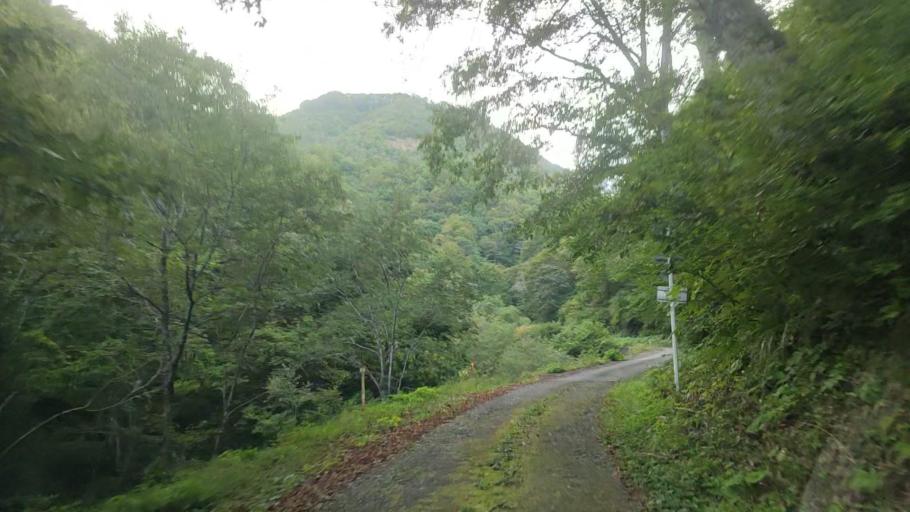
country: JP
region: Toyama
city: Yatsuomachi-higashikumisaka
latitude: 36.3336
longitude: 137.0754
